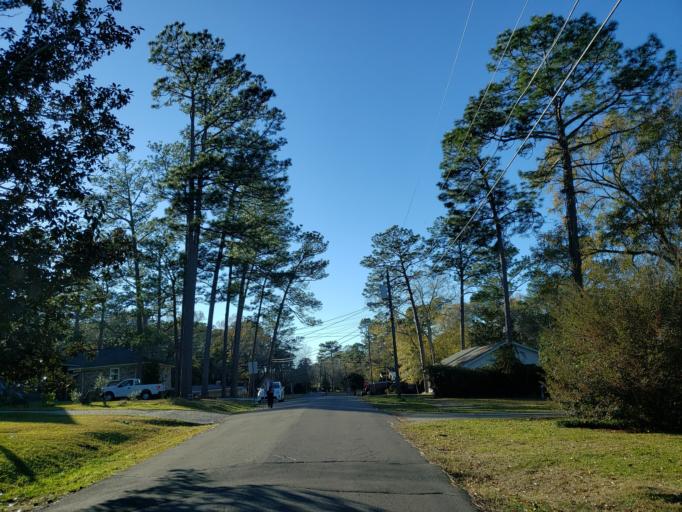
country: US
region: Mississippi
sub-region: Forrest County
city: Hattiesburg
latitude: 31.3156
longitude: -89.3176
